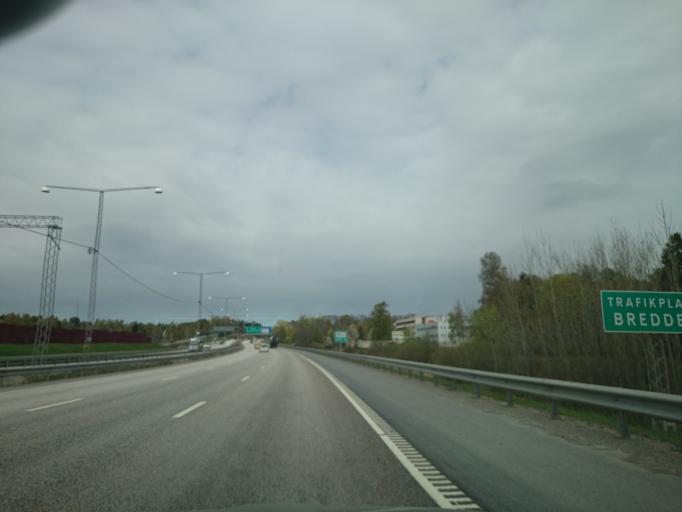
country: SE
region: Stockholm
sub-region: Upplands Vasby Kommun
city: Upplands Vaesby
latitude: 59.4812
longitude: 17.9200
